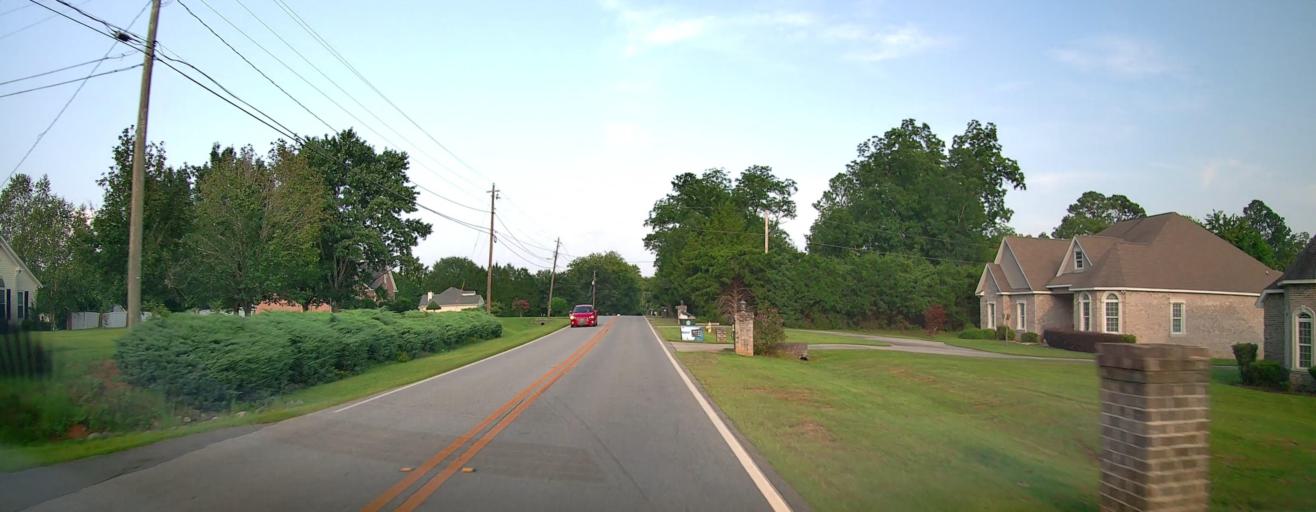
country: US
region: Georgia
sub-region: Houston County
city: Centerville
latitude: 32.7323
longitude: -83.6850
